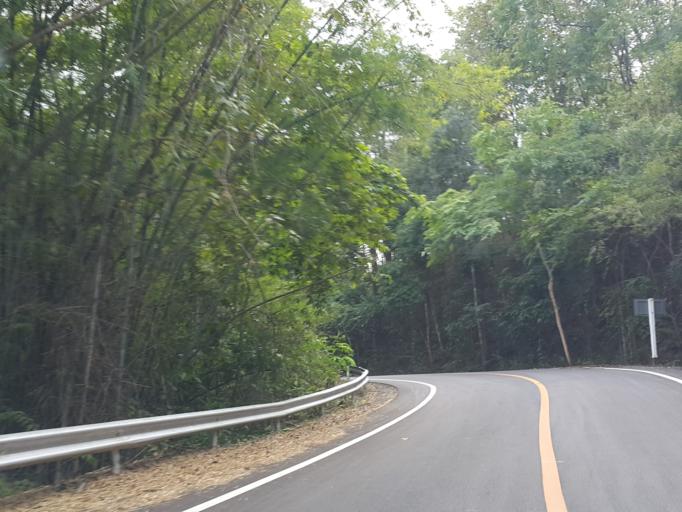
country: TH
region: Lampang
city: Chae Hom
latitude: 18.6524
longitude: 99.5226
